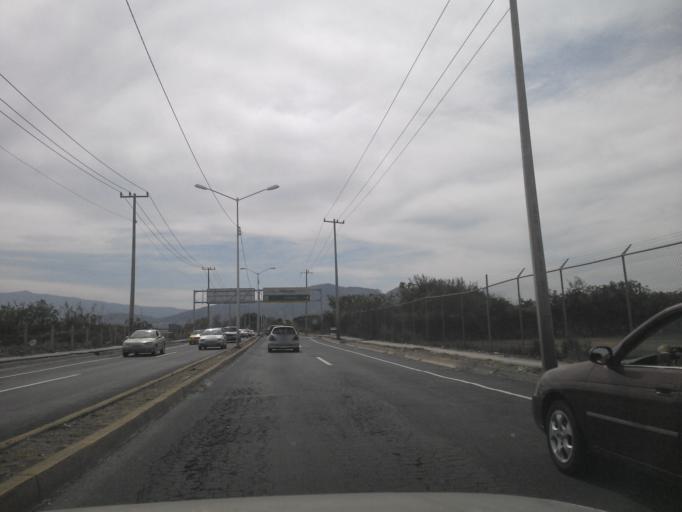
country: MX
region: Jalisco
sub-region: San Pedro Tlaquepaque
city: Paseo del Prado
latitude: 20.5520
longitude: -103.3985
